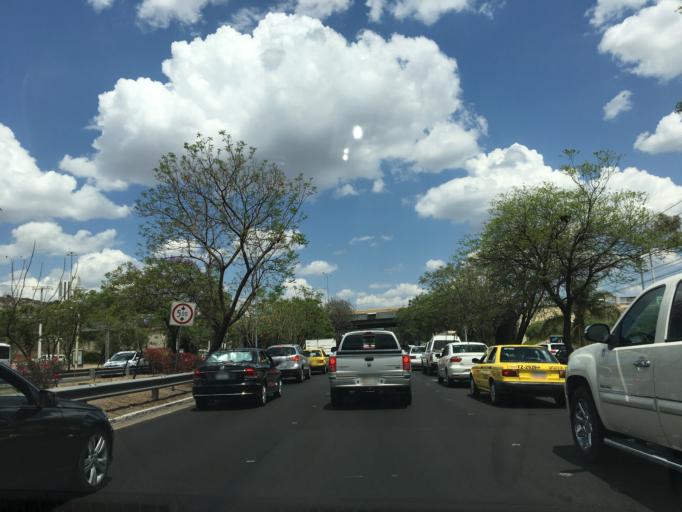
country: MX
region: Queretaro
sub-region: Queretaro
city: Santiago de Queretaro
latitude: 20.6109
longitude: -100.3820
